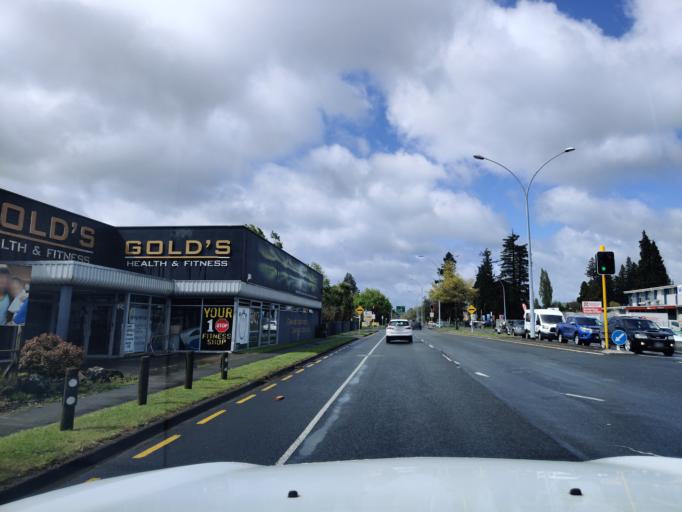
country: NZ
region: Bay of Plenty
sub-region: Rotorua District
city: Rotorua
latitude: -38.1333
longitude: 176.2343
